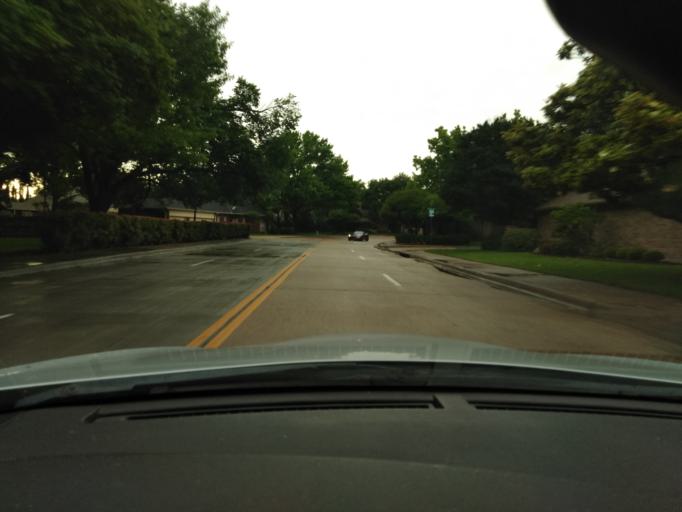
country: US
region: Texas
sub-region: Dallas County
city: Addison
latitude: 32.9907
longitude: -96.7802
